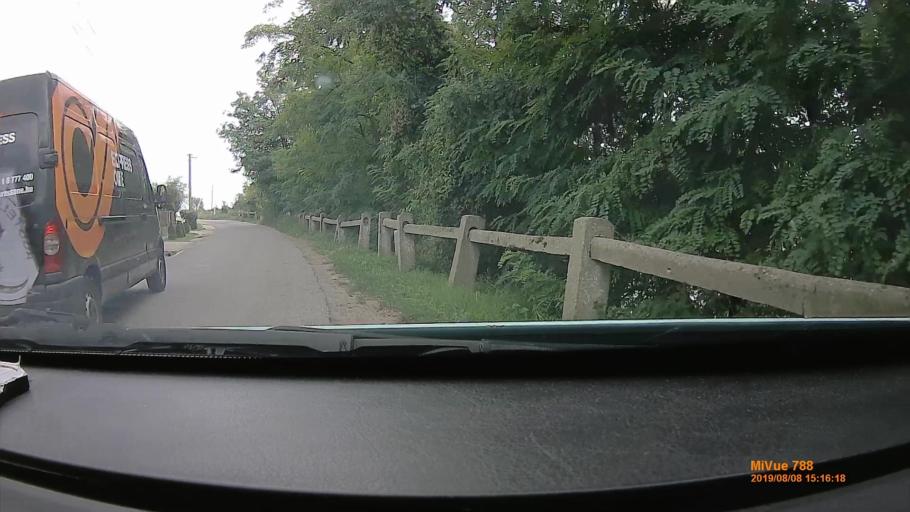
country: HU
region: Szabolcs-Szatmar-Bereg
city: Tunyogmatolcs
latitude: 47.9650
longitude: 22.4589
